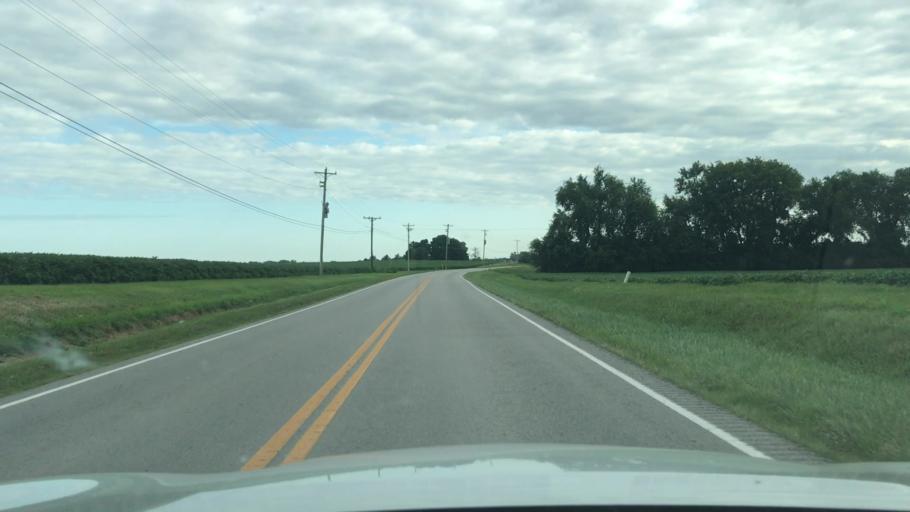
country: US
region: Kentucky
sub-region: Todd County
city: Elkton
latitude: 36.7703
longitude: -87.1667
